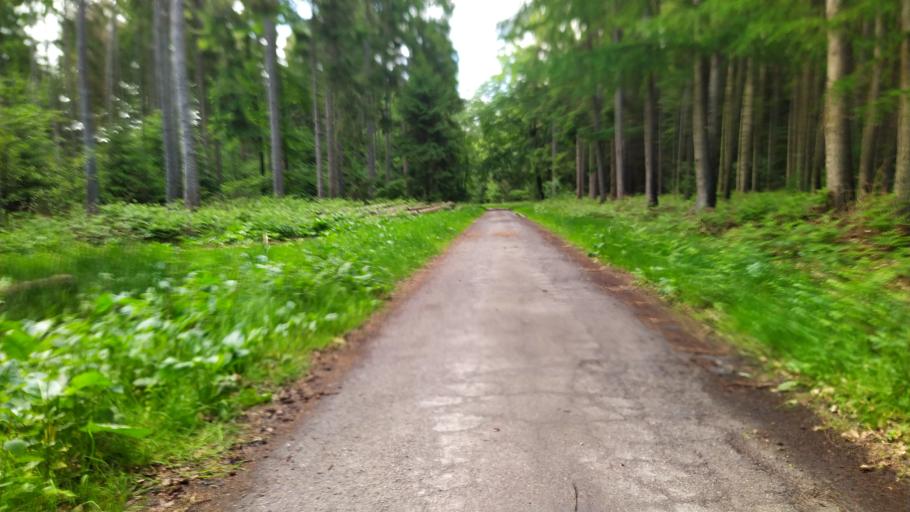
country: DE
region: Lower Saxony
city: Farven
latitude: 53.4405
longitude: 9.2862
